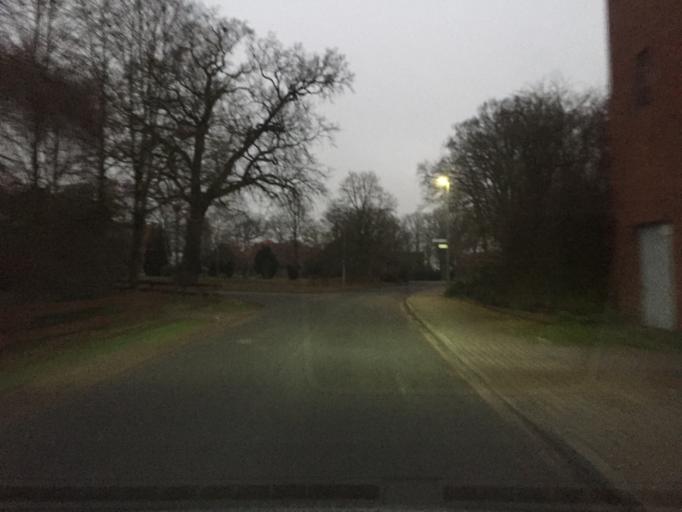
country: DE
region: Lower Saxony
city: Sulingen
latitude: 52.6689
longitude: 8.8301
